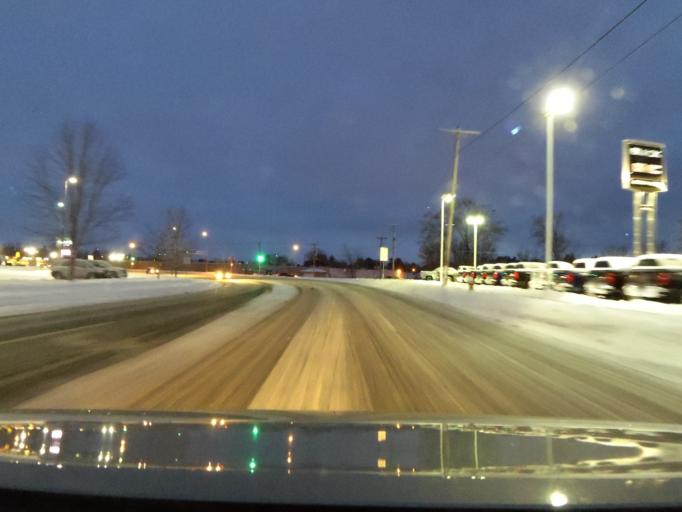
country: US
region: Wisconsin
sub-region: Dunn County
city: Menomonie
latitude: 44.9020
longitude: -91.9358
